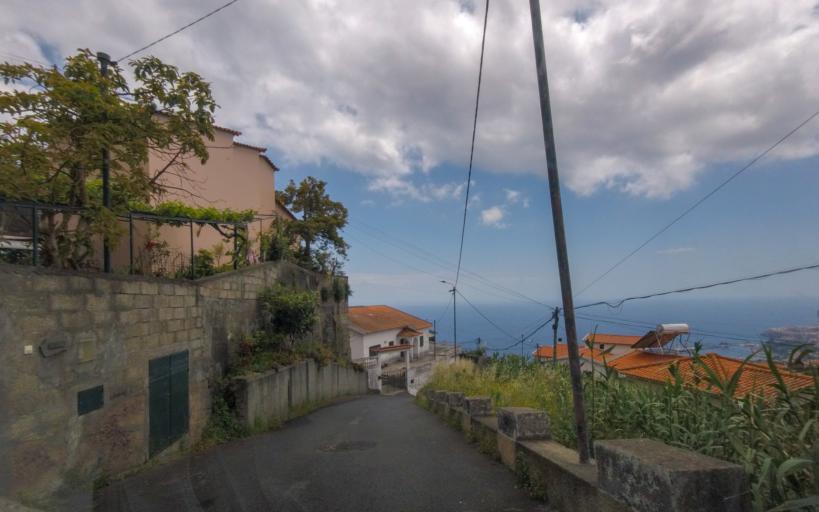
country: PT
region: Madeira
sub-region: Funchal
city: Nossa Senhora do Monte
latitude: 32.6614
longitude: -16.8816
